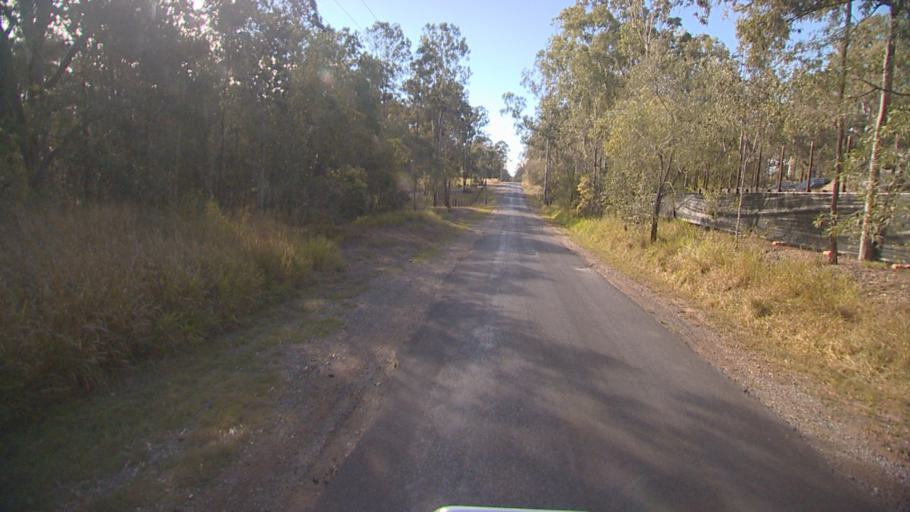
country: AU
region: Queensland
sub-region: Logan
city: Cedar Vale
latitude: -27.8320
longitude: 153.0613
